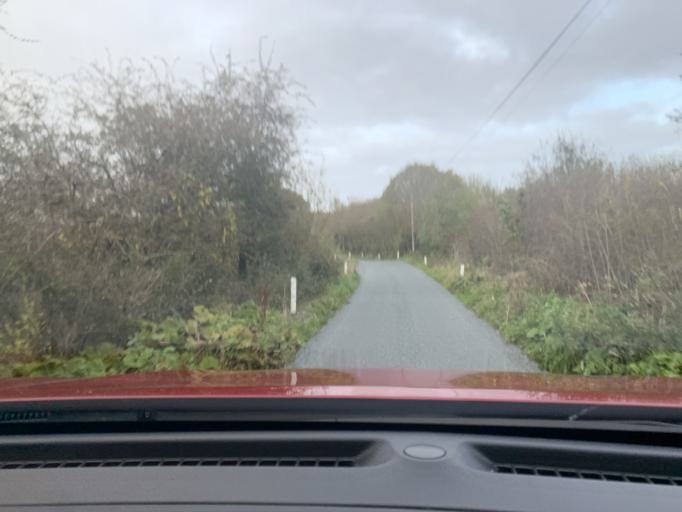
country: IE
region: Connaught
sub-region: Sligo
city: Tobercurry
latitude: 54.0688
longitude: -8.6798
